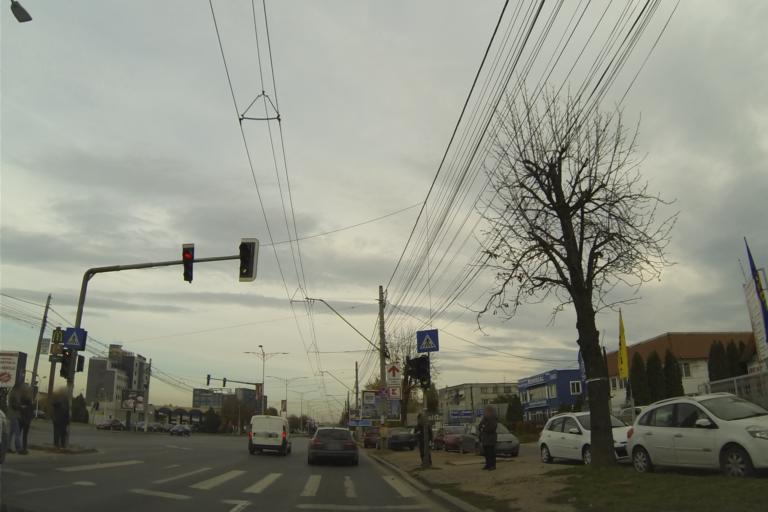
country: RO
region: Ilfov
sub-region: Comuna Chiajna
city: Chiajna
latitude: 44.4346
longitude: 25.9868
